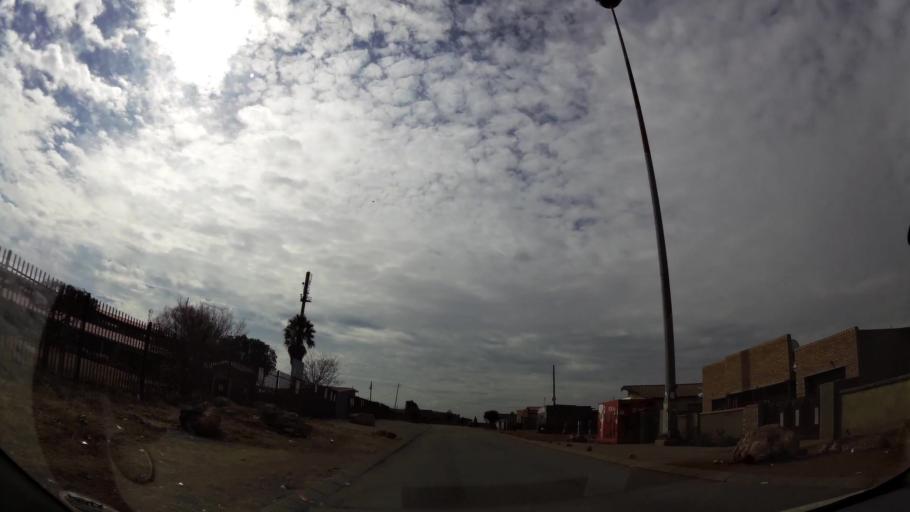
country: ZA
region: Gauteng
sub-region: Ekurhuleni Metropolitan Municipality
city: Germiston
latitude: -26.3780
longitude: 28.1647
